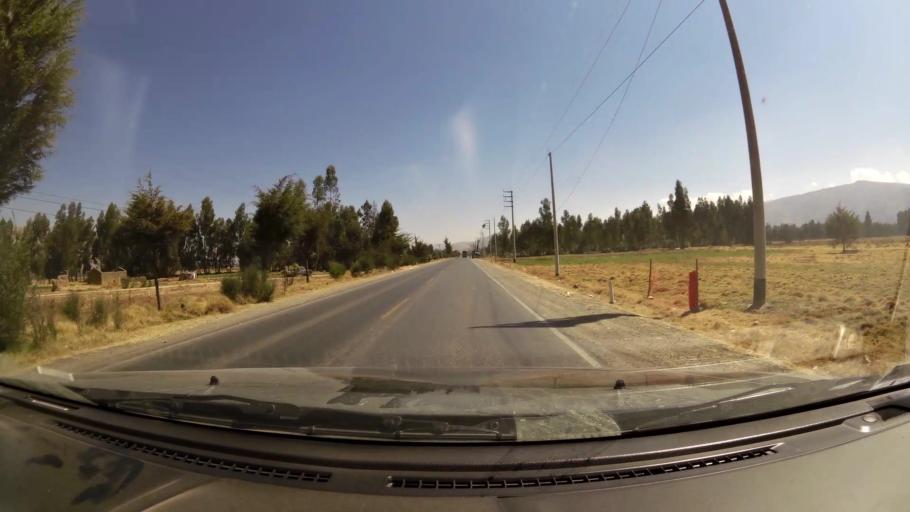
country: PE
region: Junin
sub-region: Provincia de Jauja
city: San Lorenzo
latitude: -11.8562
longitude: -75.3784
